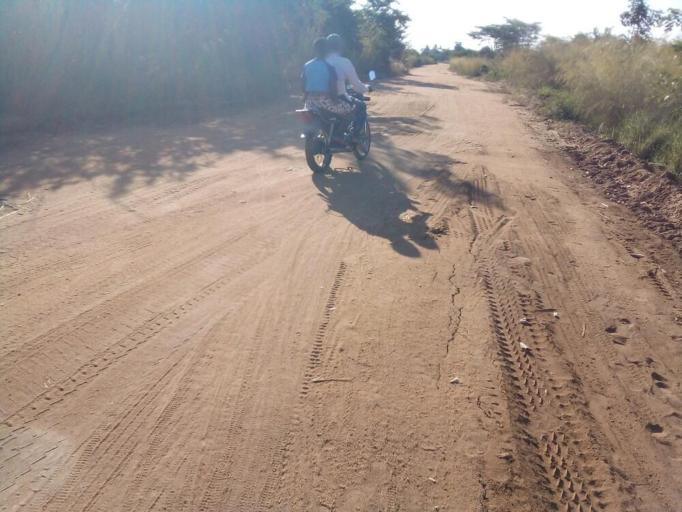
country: MZ
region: Zambezia
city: Quelimane
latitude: -17.5074
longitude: 36.8302
